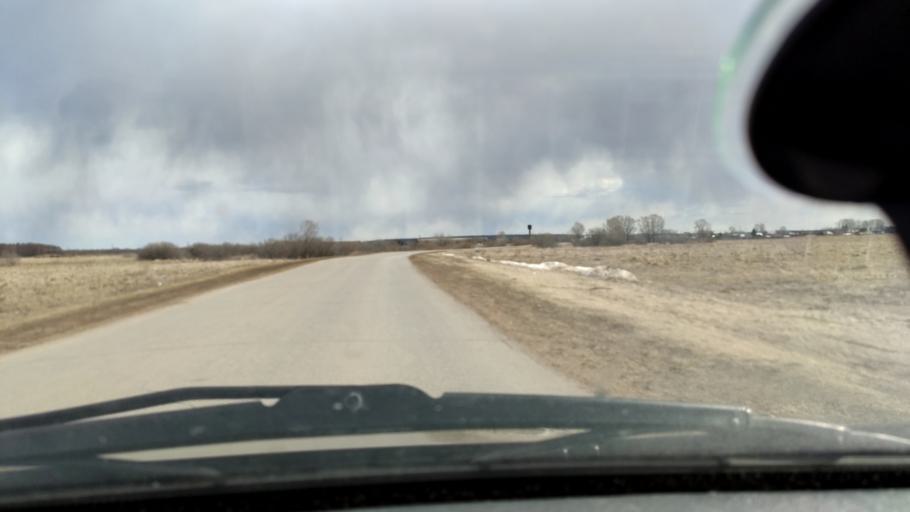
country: RU
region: Bashkortostan
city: Mikhaylovka
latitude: 54.9757
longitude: 55.7799
